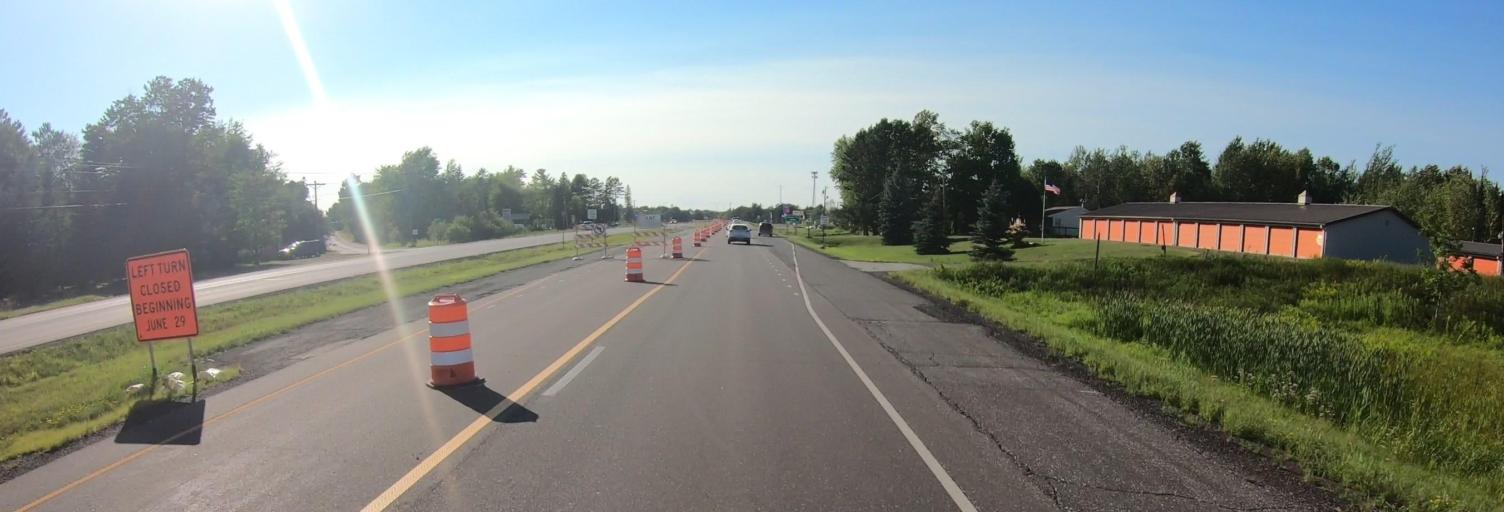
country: US
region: Minnesota
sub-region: Saint Louis County
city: Hermantown
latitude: 46.8486
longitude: -92.2749
